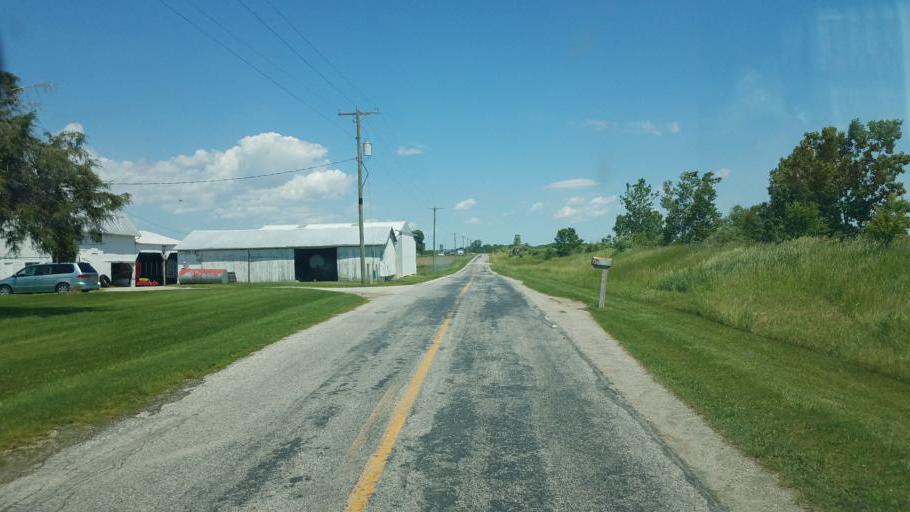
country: US
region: Ohio
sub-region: Hardin County
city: Forest
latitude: 40.6779
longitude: -83.4197
